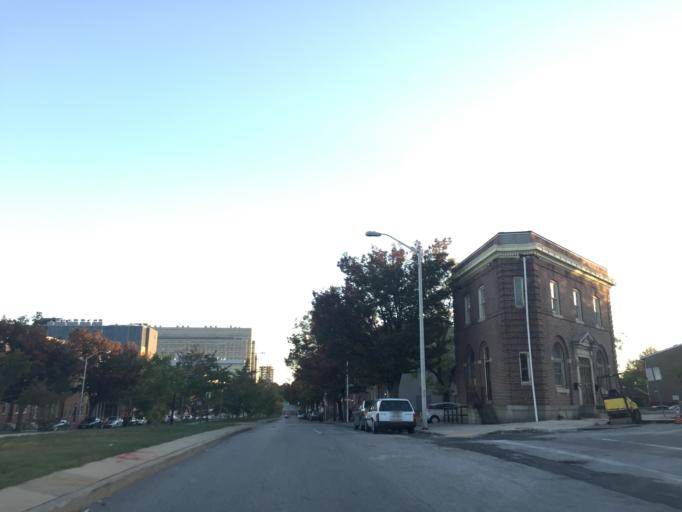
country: US
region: Maryland
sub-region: City of Baltimore
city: Baltimore
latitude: 39.3037
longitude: -76.5947
